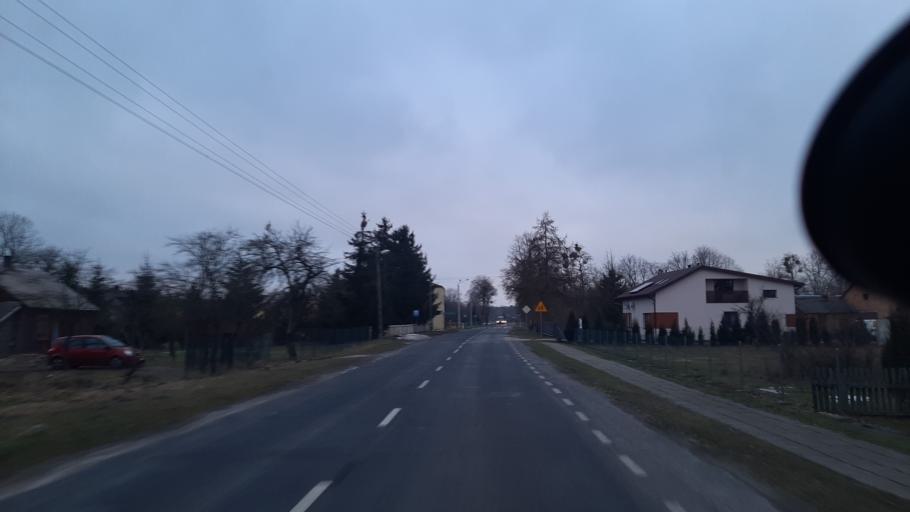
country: PL
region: Lublin Voivodeship
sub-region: Powiat parczewski
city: Debowa Kloda
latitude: 51.6381
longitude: 23.0373
